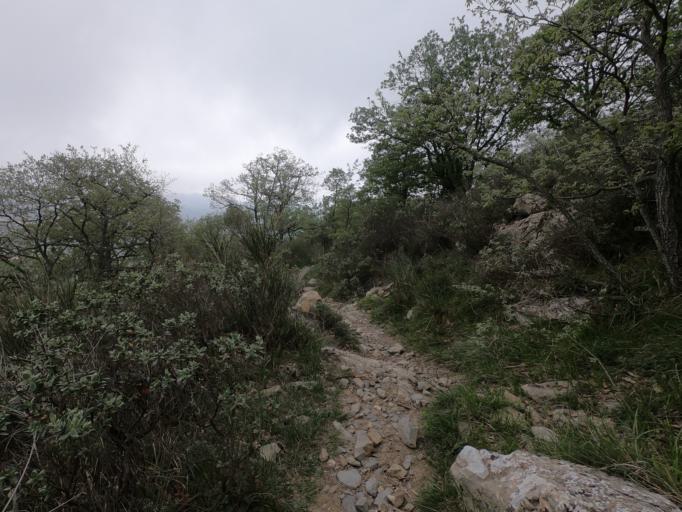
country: IT
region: Liguria
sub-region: Provincia di Imperia
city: Villa Faraldi
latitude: 43.9726
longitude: 8.0885
